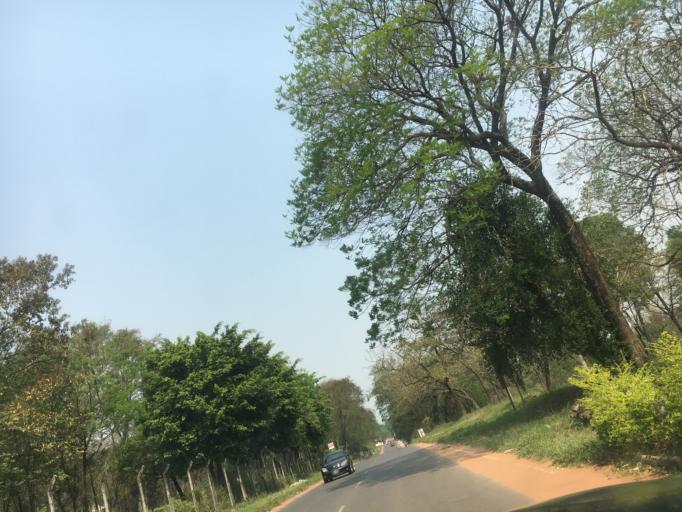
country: PY
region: Central
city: Villa Elisa
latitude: -25.3761
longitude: -57.5906
